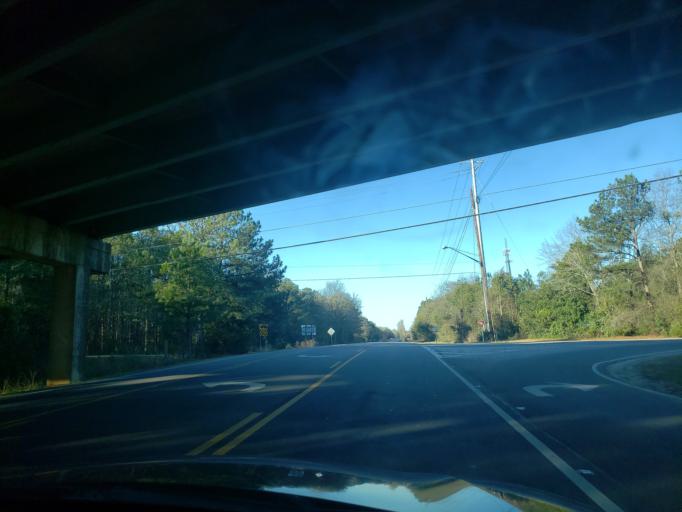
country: US
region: Alabama
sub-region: Lee County
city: Auburn
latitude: 32.6079
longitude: -85.5079
